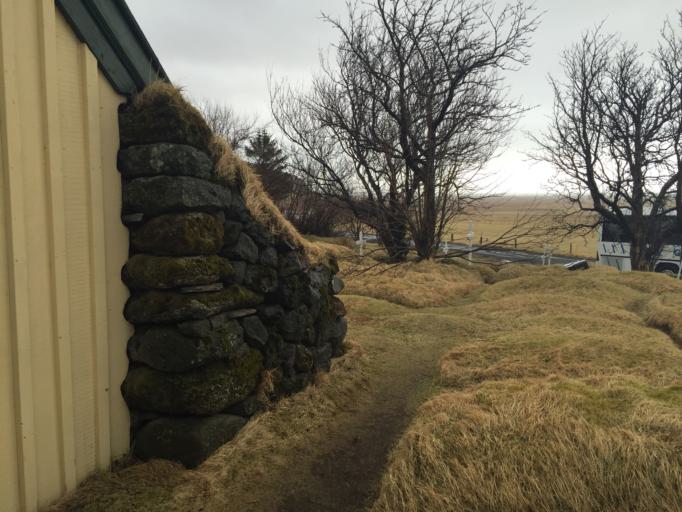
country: IS
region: East
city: Hoefn
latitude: 63.9070
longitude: -16.7069
